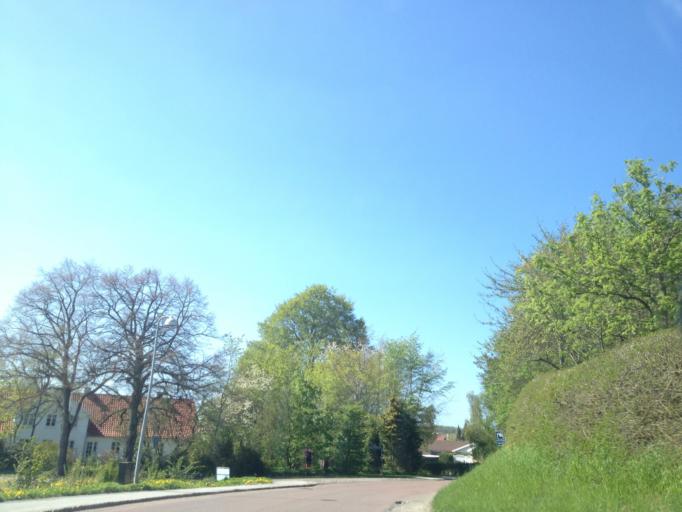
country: DK
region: Zealand
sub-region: Koge Kommune
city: Borup
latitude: 55.4835
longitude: 11.8871
